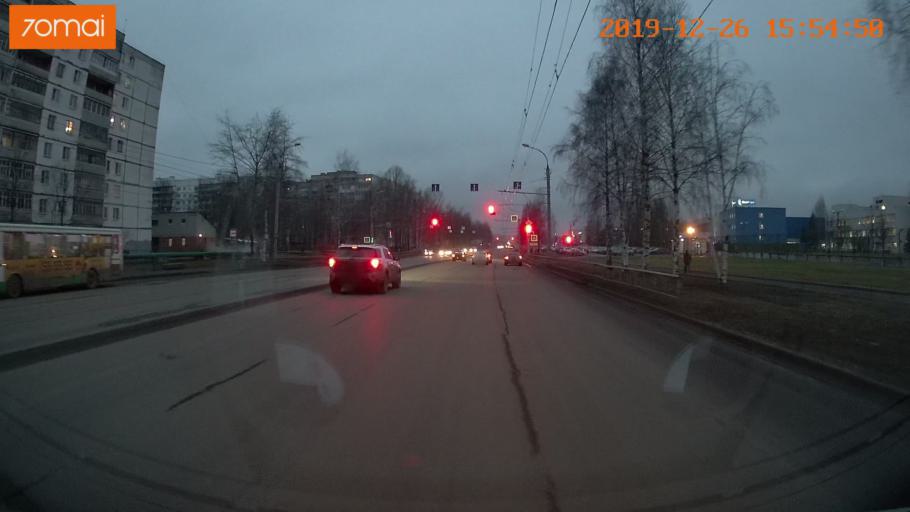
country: RU
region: Jaroslavl
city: Rybinsk
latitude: 58.0435
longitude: 38.8140
